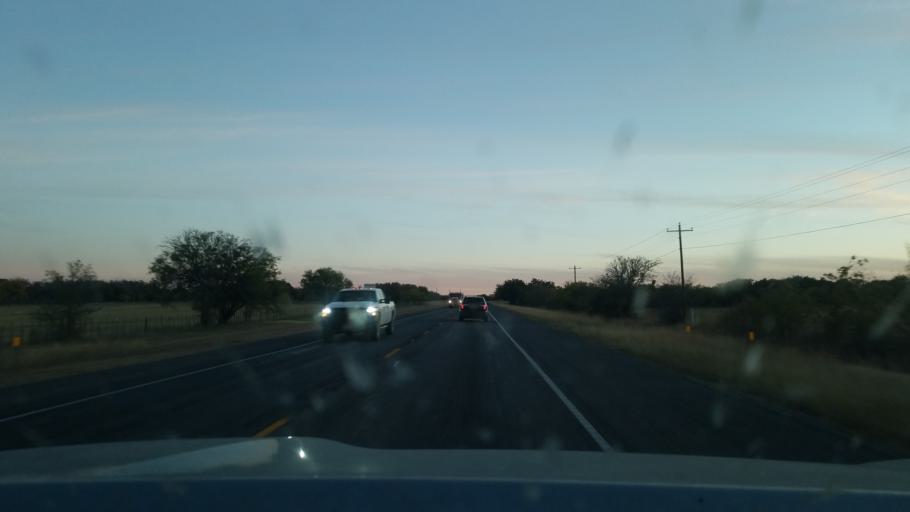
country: US
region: Texas
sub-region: Stephens County
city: Breckenridge
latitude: 32.5879
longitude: -98.8978
